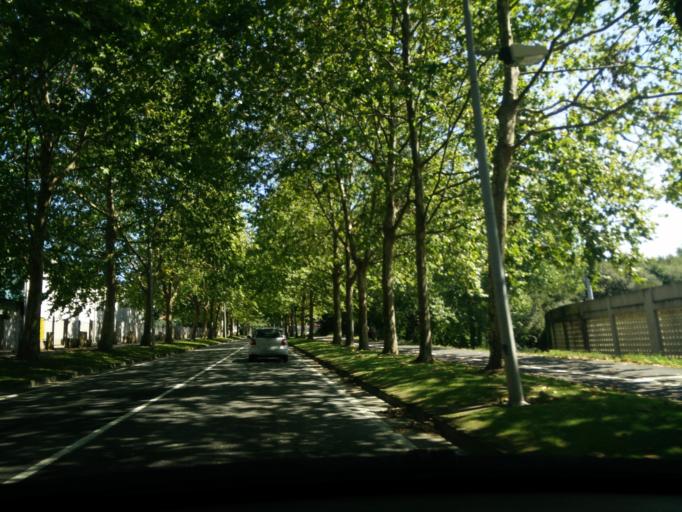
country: ES
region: Galicia
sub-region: Provincia da Coruna
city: Oleiros
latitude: 43.3397
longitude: -8.3567
